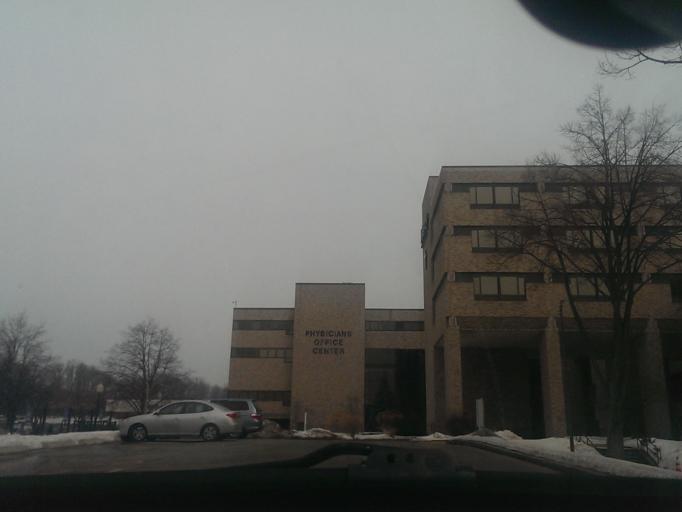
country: US
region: Massachusetts
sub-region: Hampden County
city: Springfield
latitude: 42.1152
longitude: -72.5943
